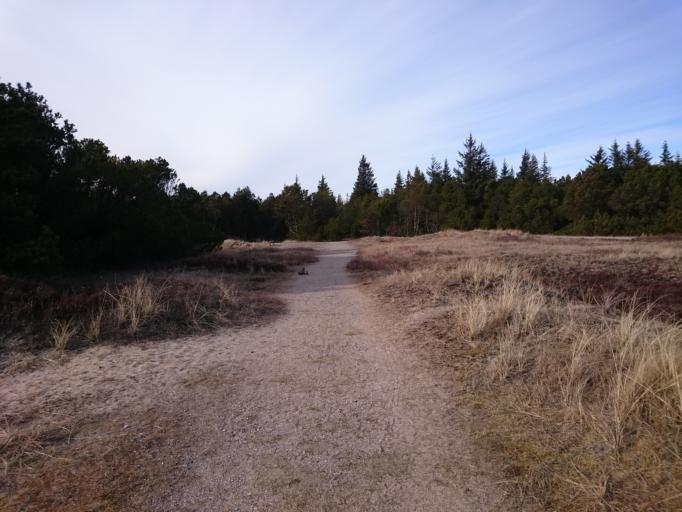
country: DK
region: North Denmark
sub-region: Frederikshavn Kommune
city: Skagen
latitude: 57.6972
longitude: 10.5217
